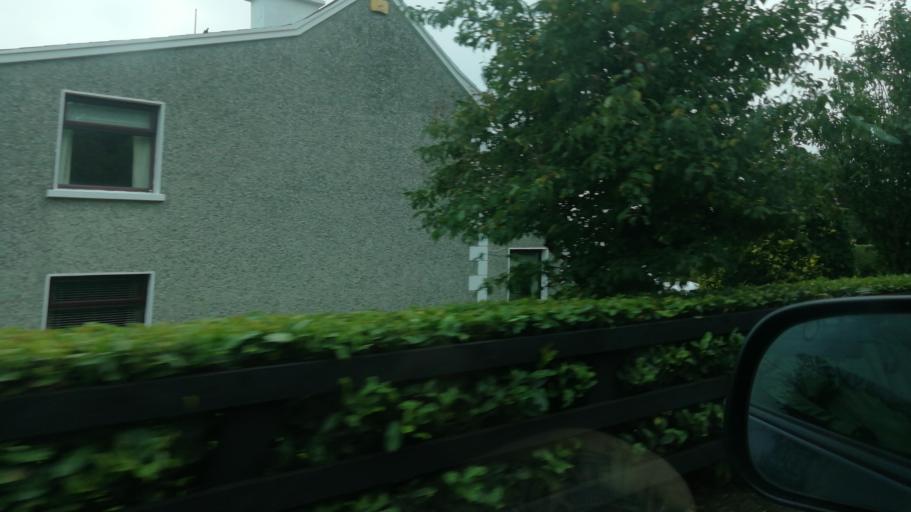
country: IE
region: Munster
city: Fethard
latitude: 52.5447
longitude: -7.6804
